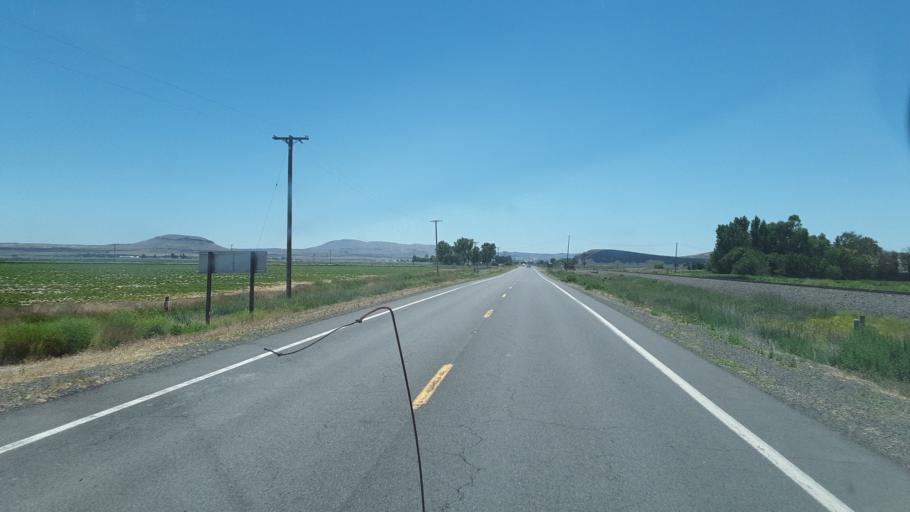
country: US
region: California
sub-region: Siskiyou County
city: Tulelake
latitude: 41.9151
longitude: -121.4236
